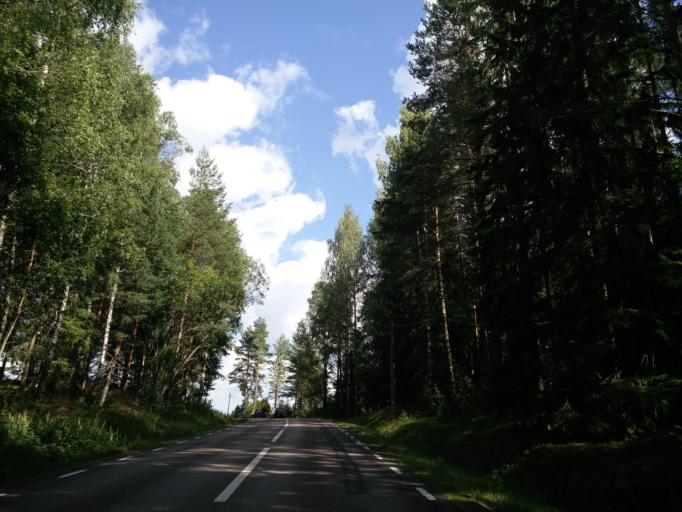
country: SE
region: Vaermland
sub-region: Sunne Kommun
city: Sunne
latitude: 59.6677
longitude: 12.9722
